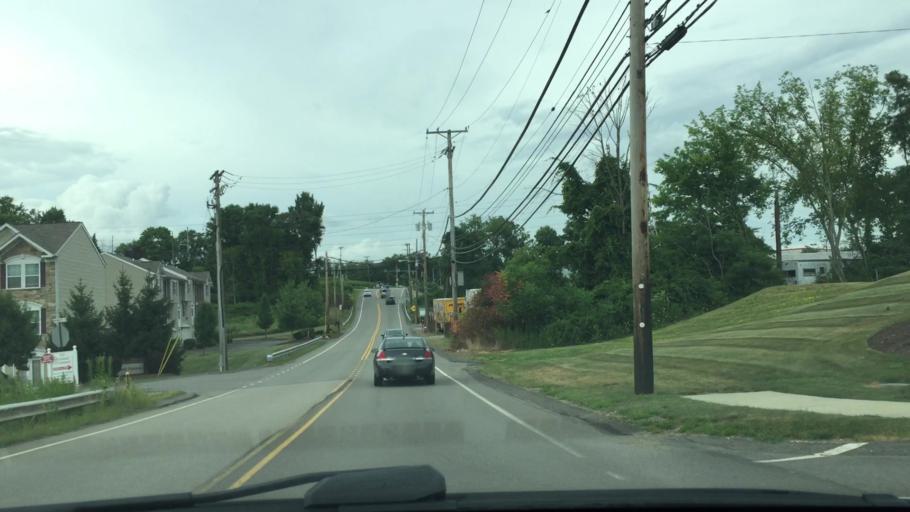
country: US
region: Pennsylvania
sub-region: Allegheny County
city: McKees Rocks
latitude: 40.4660
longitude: -80.0996
